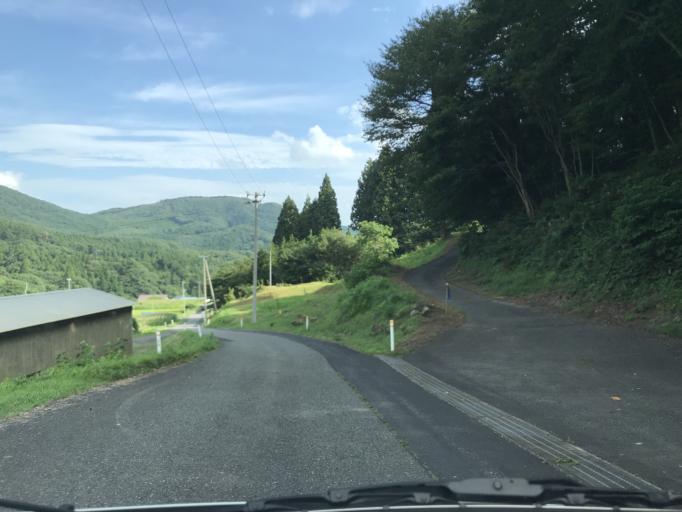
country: JP
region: Iwate
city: Ofunato
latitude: 38.9669
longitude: 141.4706
